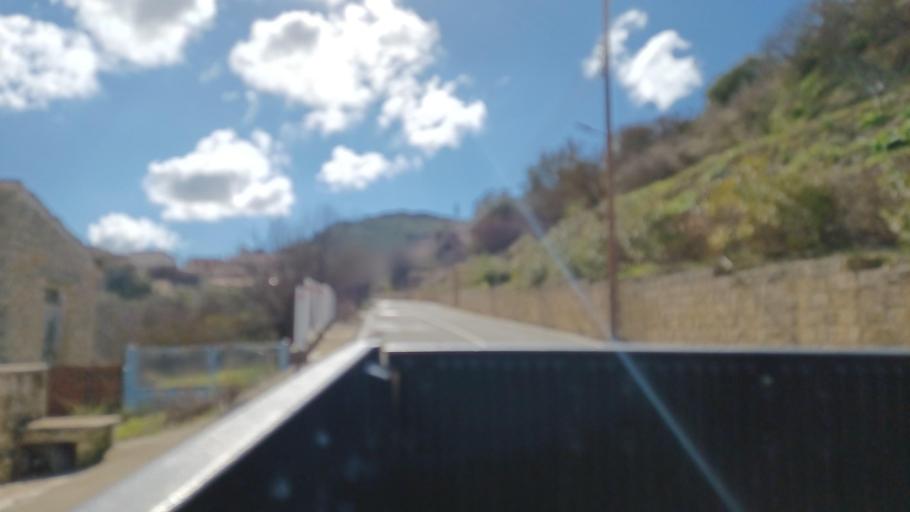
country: CY
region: Limassol
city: Pachna
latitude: 34.7832
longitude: 32.7380
